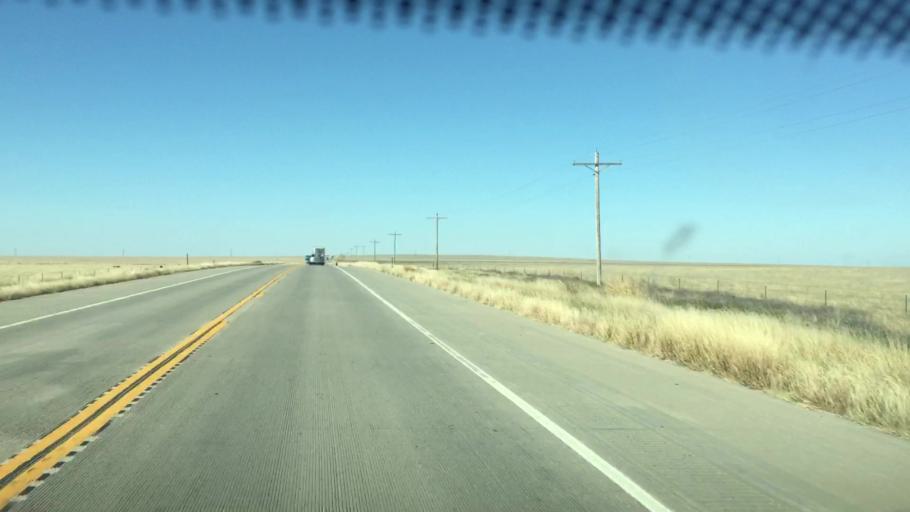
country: US
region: Colorado
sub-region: Prowers County
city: Lamar
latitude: 38.2409
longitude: -102.7240
